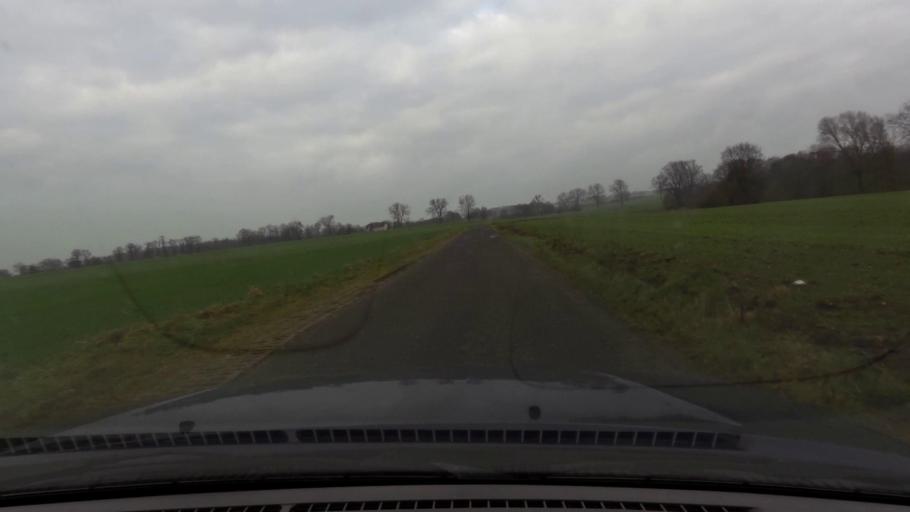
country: PL
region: West Pomeranian Voivodeship
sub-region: Powiat stargardzki
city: Stargard Szczecinski
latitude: 53.3446
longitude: 15.1256
